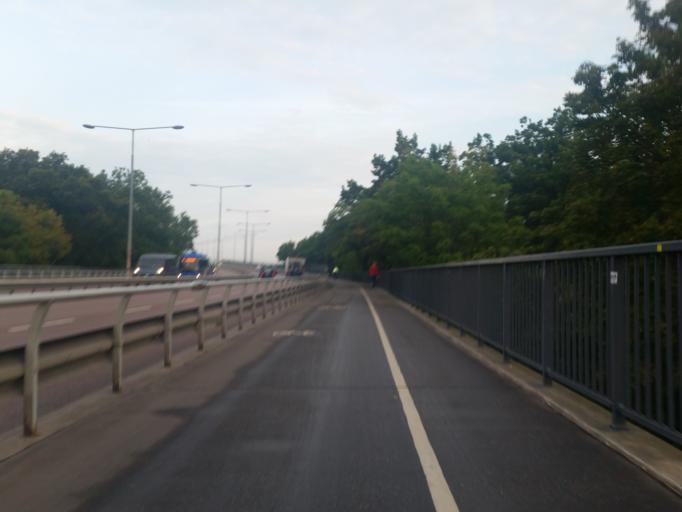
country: SE
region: Stockholm
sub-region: Stockholms Kommun
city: Arsta
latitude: 59.3208
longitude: 18.0313
